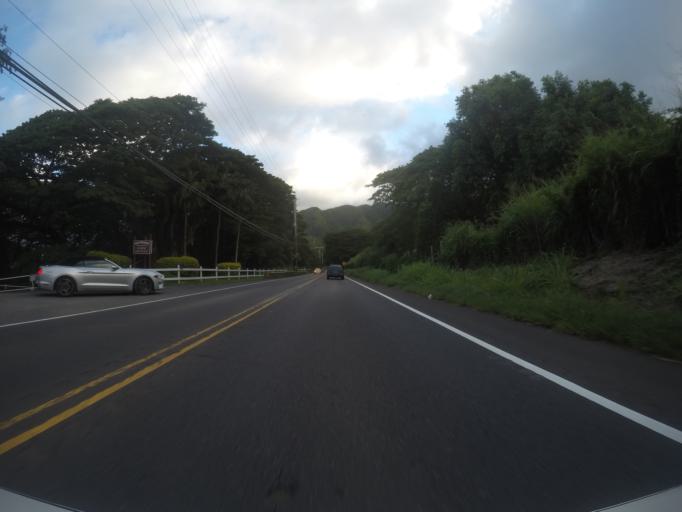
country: US
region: Hawaii
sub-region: Honolulu County
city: Ka'a'awa
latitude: 21.5112
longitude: -157.8518
